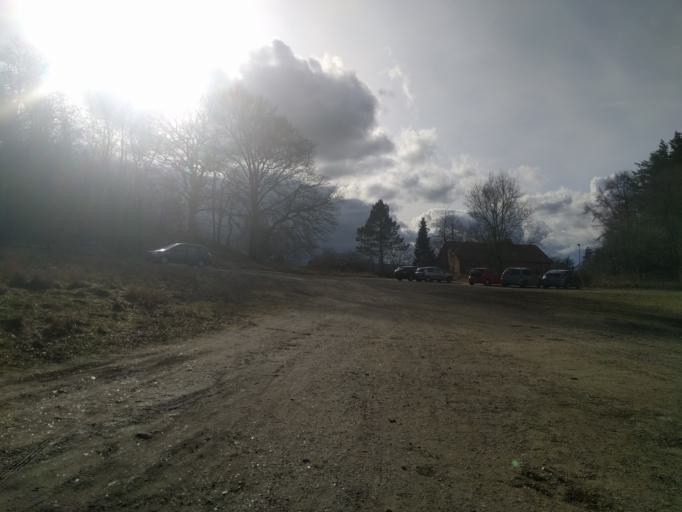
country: DK
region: Central Jutland
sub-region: Viborg Kommune
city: Viborg
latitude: 56.4394
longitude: 9.4282
